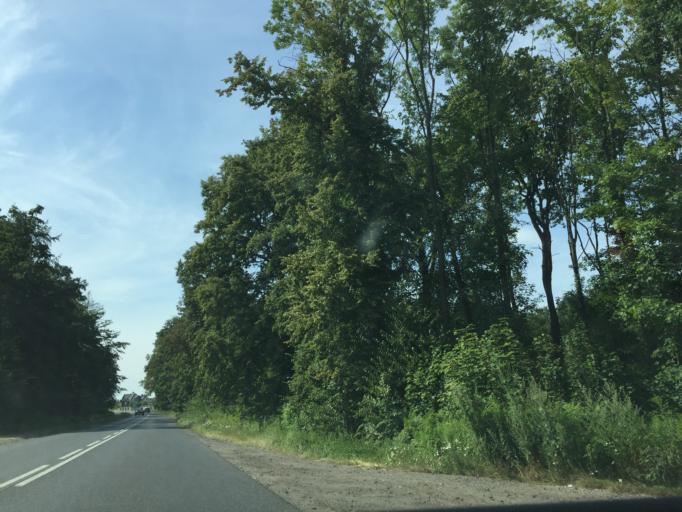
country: PL
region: Silesian Voivodeship
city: Gorzyczki
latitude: 49.9472
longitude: 18.4199
